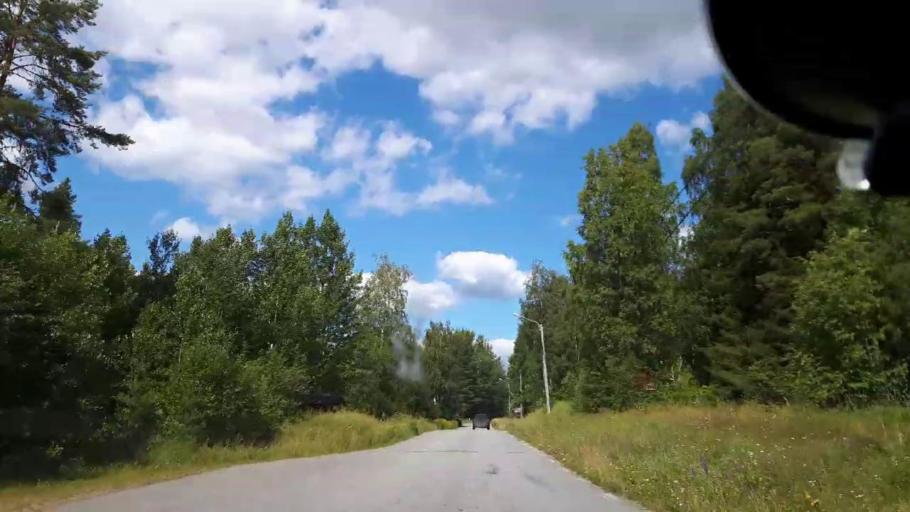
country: SE
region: Jaemtland
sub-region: Ragunda Kommun
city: Hammarstrand
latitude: 62.9481
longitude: 16.6887
